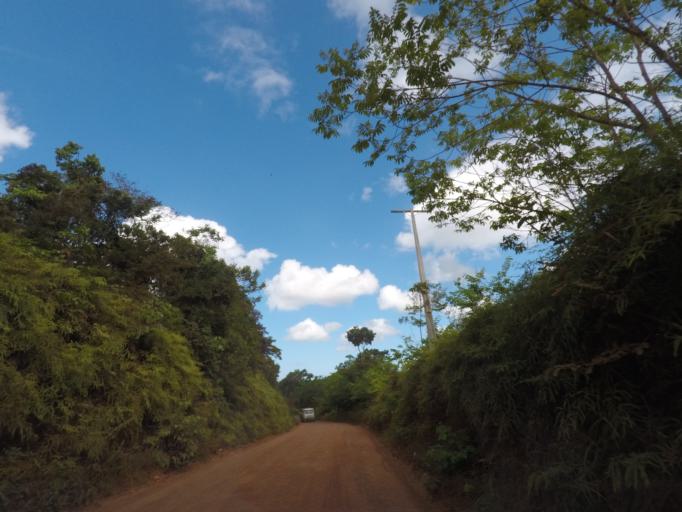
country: BR
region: Bahia
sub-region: Itacare
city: Itacare
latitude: -14.2202
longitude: -39.0914
